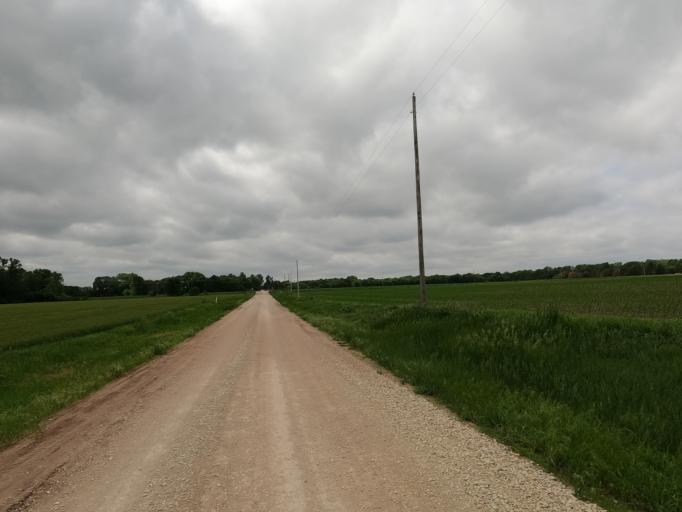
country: US
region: Kansas
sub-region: McPherson County
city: McPherson
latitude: 38.2920
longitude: -97.6121
